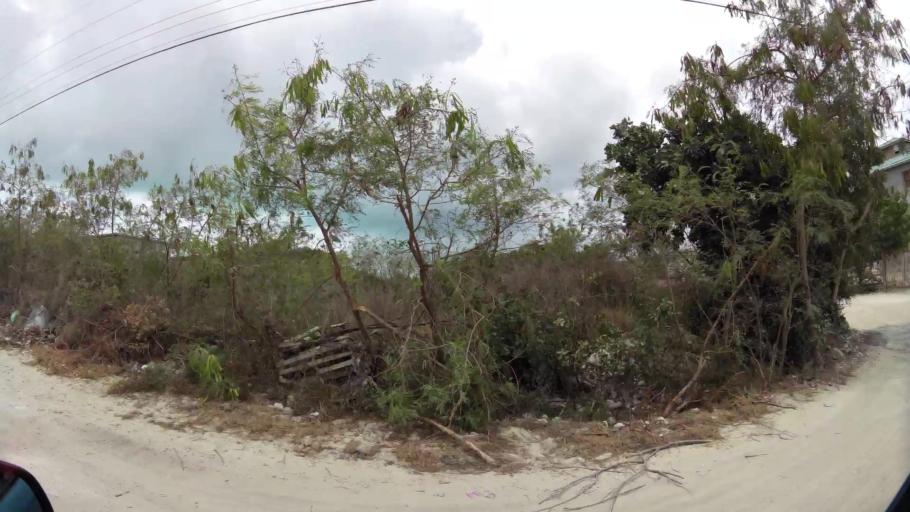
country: BS
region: Mayaguana
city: Abraham's Bay
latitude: 21.7853
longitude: -72.2587
